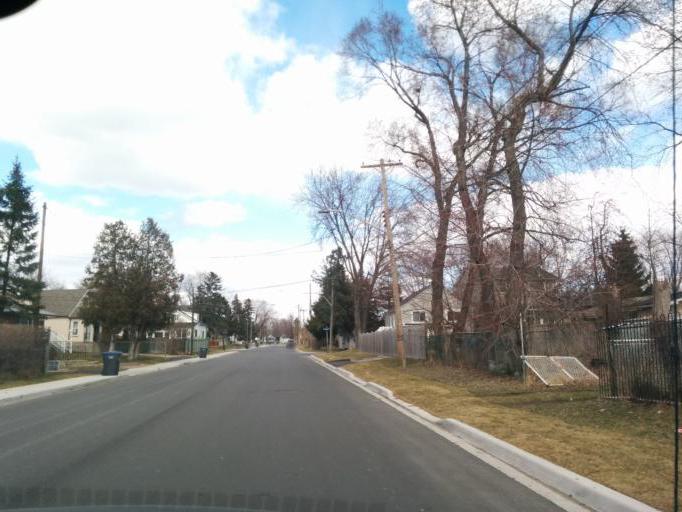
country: CA
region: Ontario
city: Etobicoke
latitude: 43.5749
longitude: -79.5651
